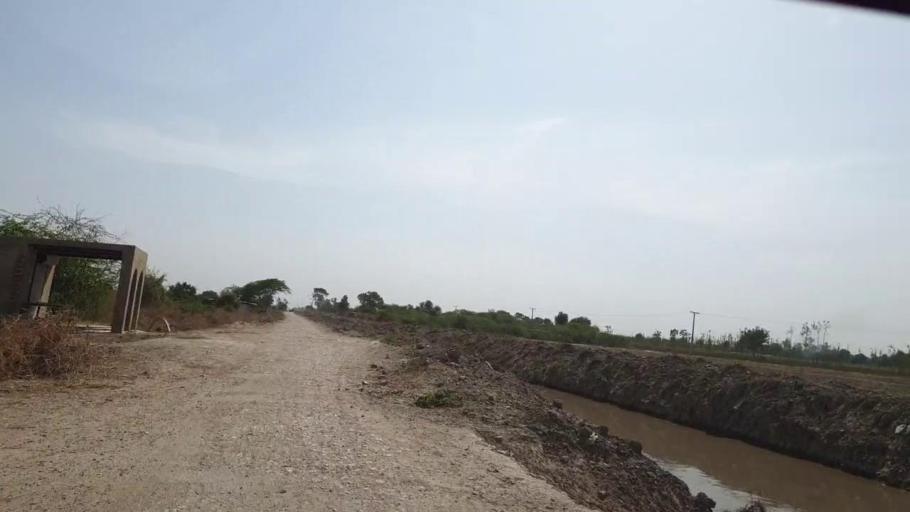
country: PK
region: Sindh
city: Nabisar
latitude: 25.0785
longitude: 69.5797
